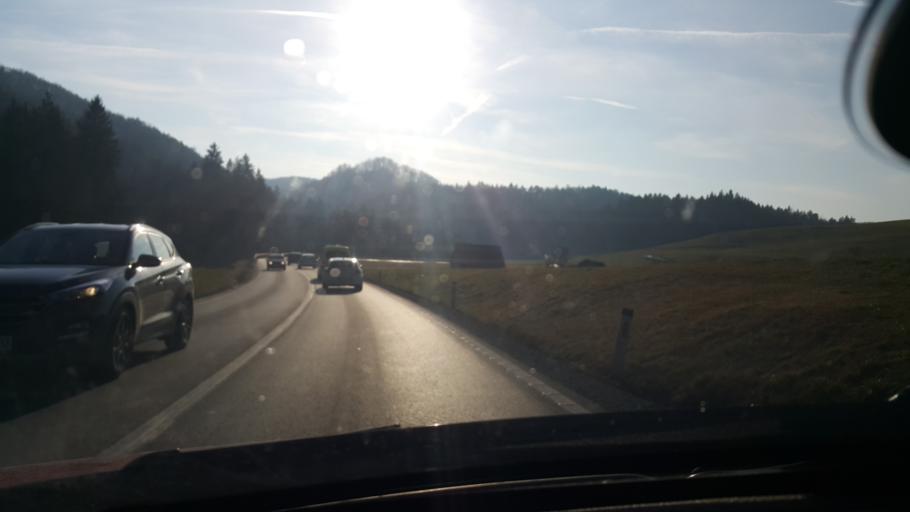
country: SI
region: Dobrna
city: Dobrna
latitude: 46.3212
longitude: 15.1806
